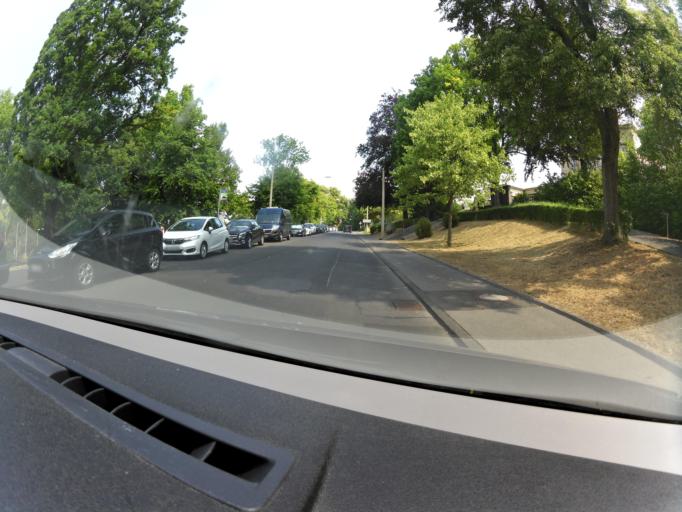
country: DE
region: Bavaria
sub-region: Regierungsbezirk Unterfranken
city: Bad Kissingen
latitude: 50.1914
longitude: 10.0783
